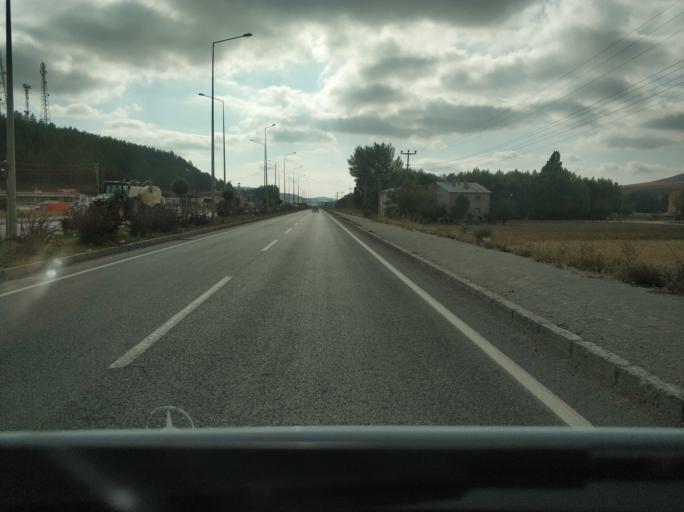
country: TR
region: Sivas
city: Yildizeli
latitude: 39.8717
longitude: 36.6067
